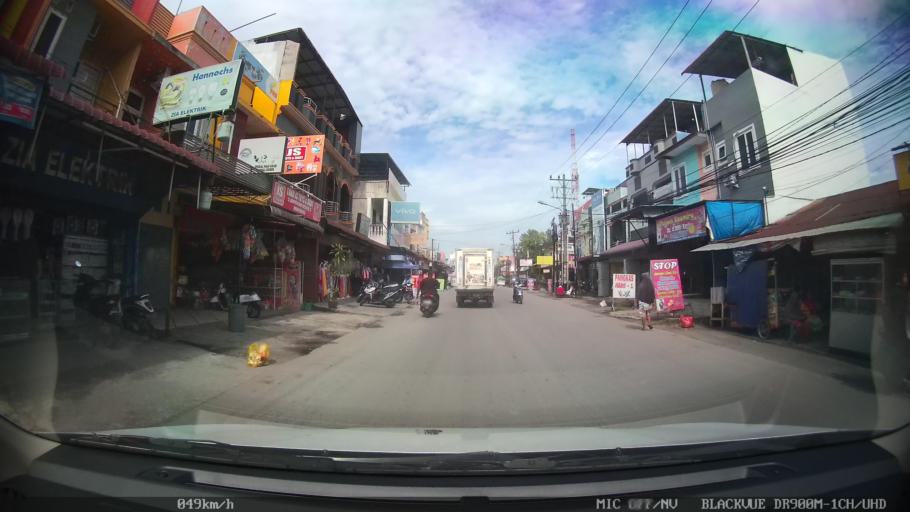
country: ID
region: North Sumatra
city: Sunggal
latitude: 3.6088
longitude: 98.6108
